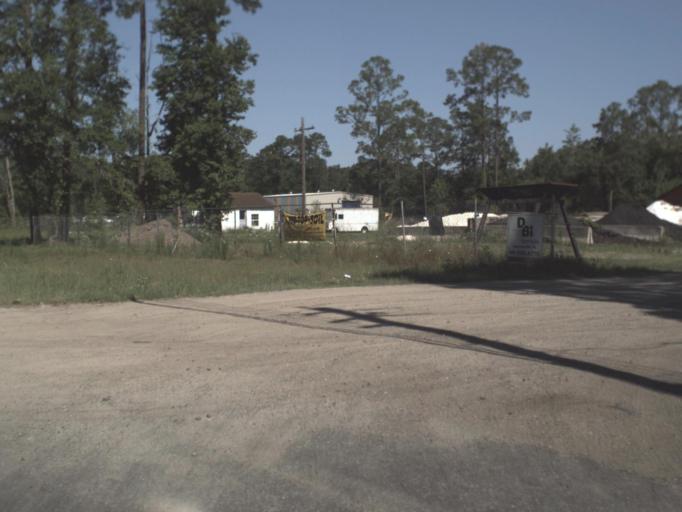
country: US
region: Florida
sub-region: Duval County
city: Jacksonville
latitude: 30.3197
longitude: -81.7992
